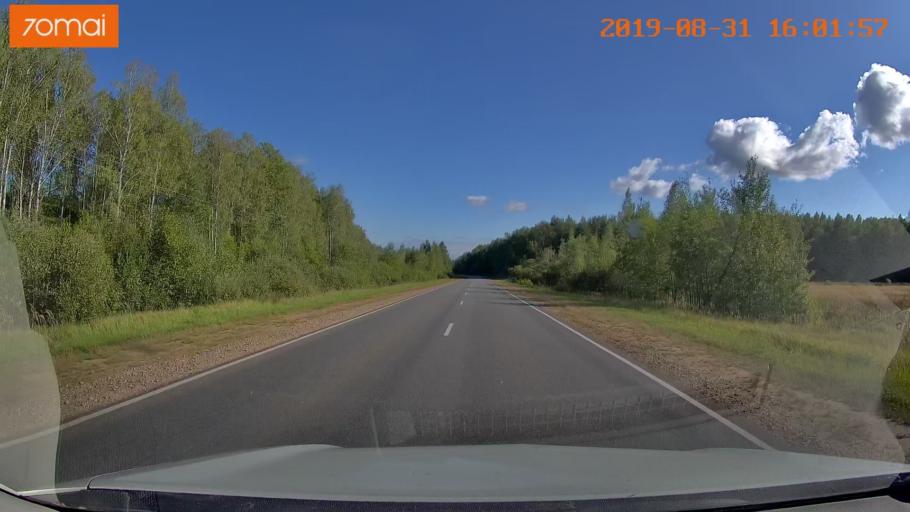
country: RU
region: Kaluga
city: Yukhnov
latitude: 54.6819
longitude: 35.2956
